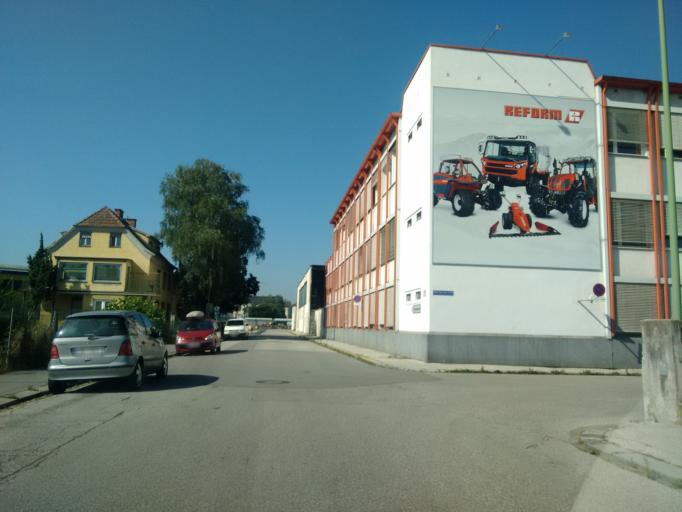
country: AT
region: Upper Austria
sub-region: Wels Stadt
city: Wels
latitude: 48.1668
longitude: 14.0185
